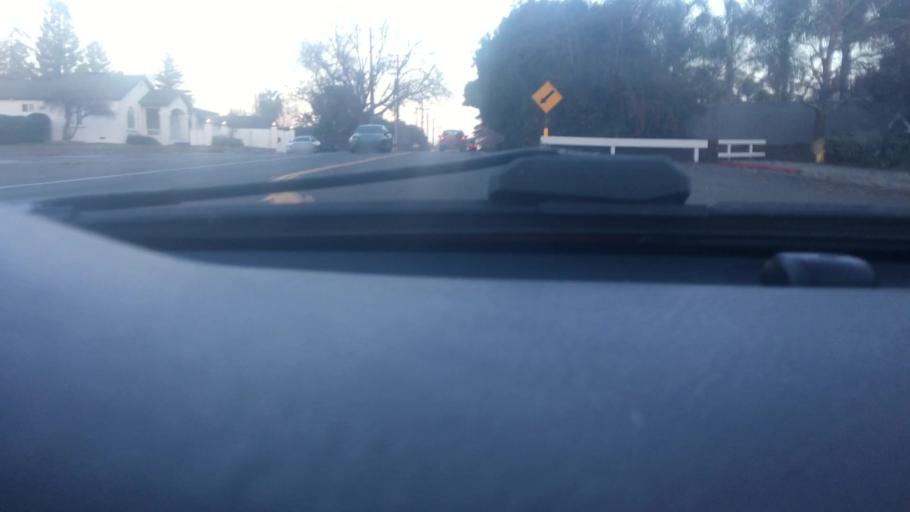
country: US
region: California
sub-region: Sacramento County
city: Carmichael
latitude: 38.6391
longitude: -121.3452
